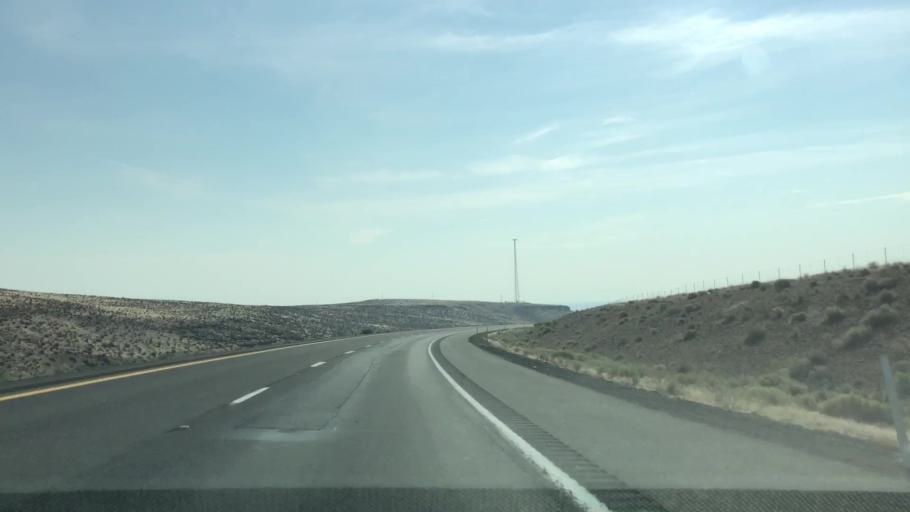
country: US
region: Washington
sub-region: Grant County
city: Mattawa
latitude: 46.9447
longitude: -120.0932
